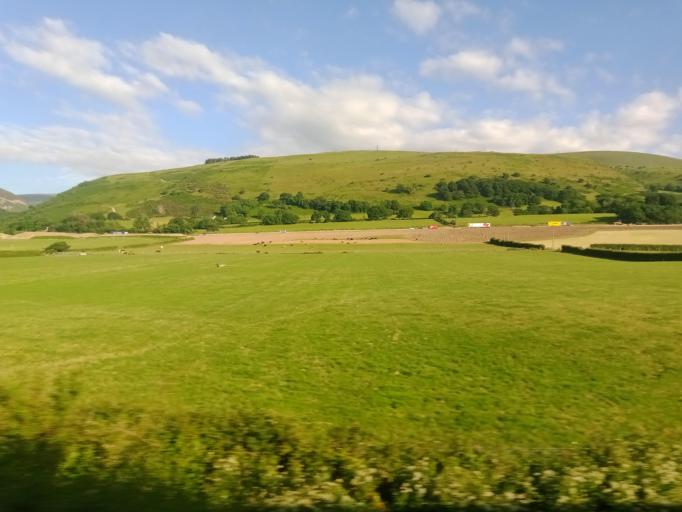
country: GB
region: Wales
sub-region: Gwynedd
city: Aber
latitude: 53.2359
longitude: -4.0298
